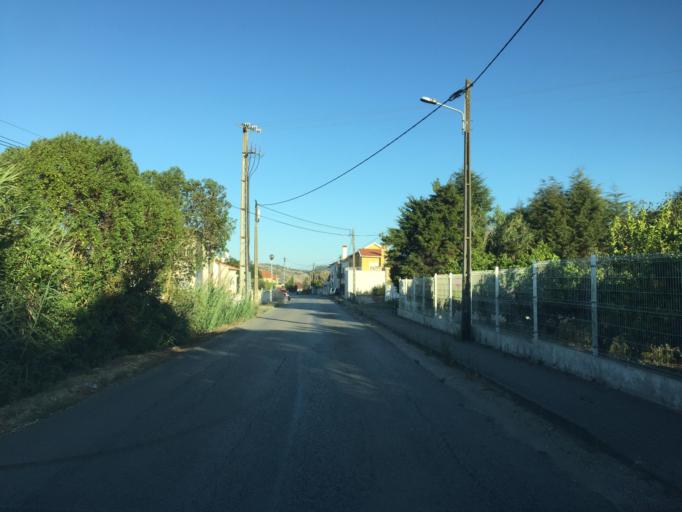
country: PT
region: Lisbon
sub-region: Torres Vedras
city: Torres Vedras
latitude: 39.0880
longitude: -9.2722
